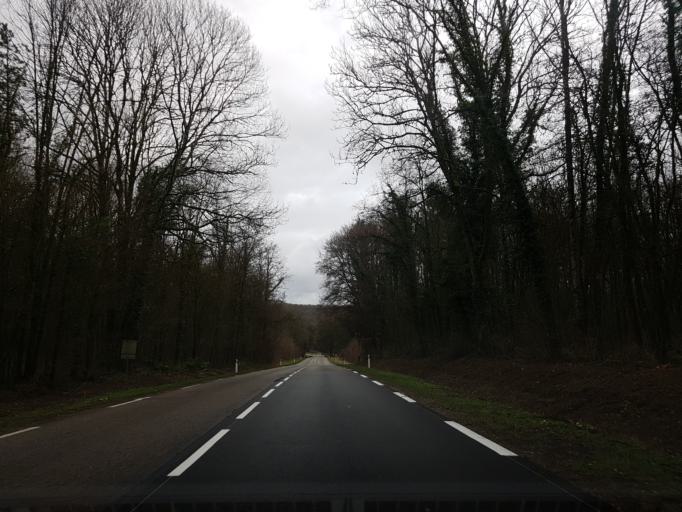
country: FR
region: Franche-Comte
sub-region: Departement de la Haute-Saone
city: Scey-sur-Saone-et-Saint-Albin
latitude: 47.6908
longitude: 5.9920
